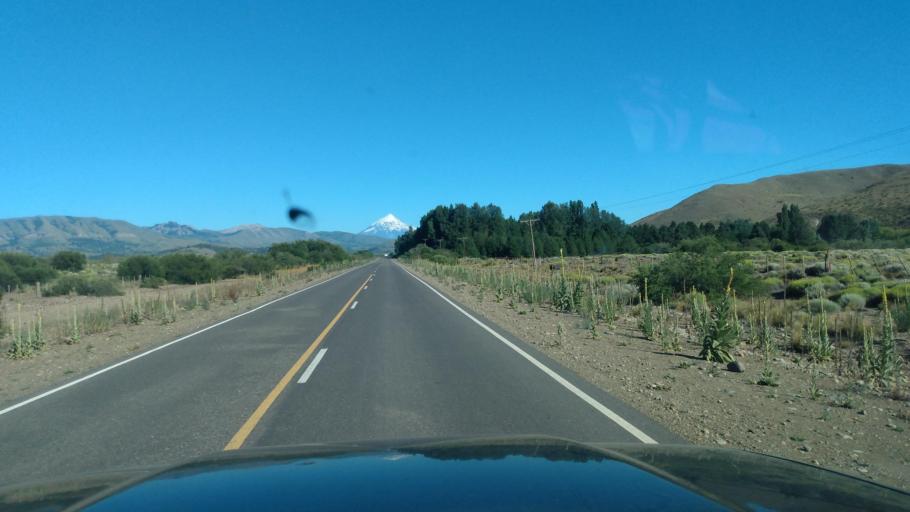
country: AR
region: Neuquen
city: Junin de los Andes
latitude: -39.8998
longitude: -71.1404
